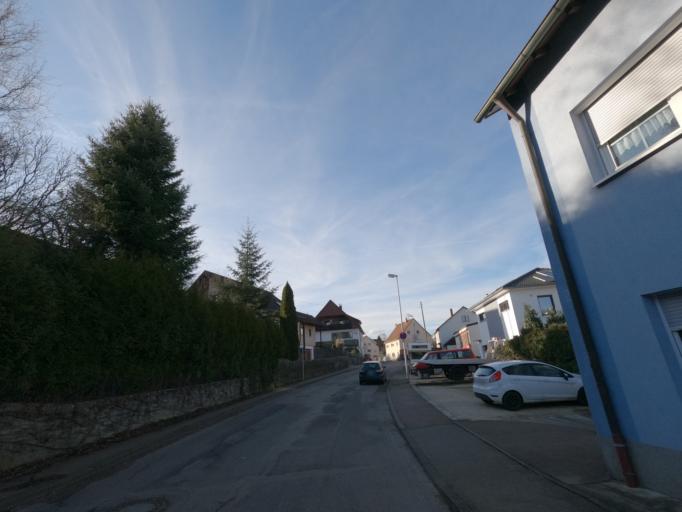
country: DE
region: Baden-Wuerttemberg
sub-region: Regierungsbezirk Stuttgart
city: Donzdorf
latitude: 48.7089
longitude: 9.7949
